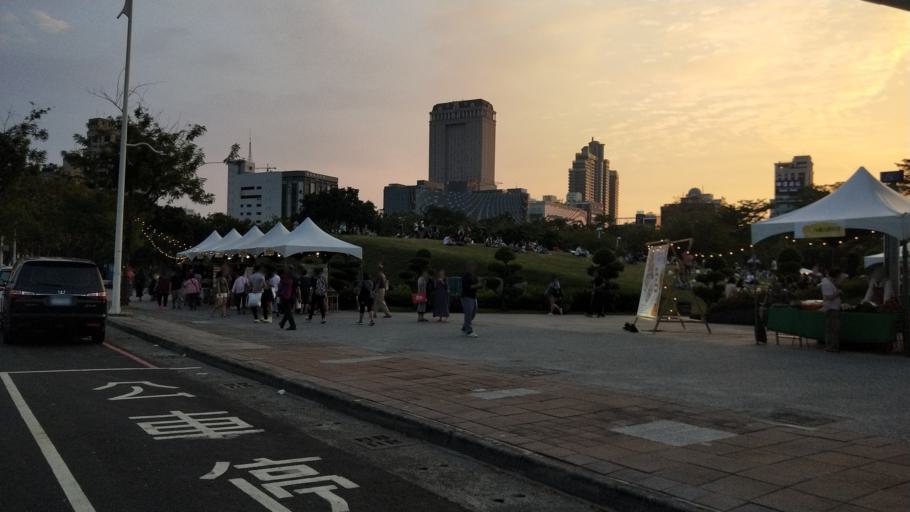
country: TW
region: Kaohsiung
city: Kaohsiung
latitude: 22.6247
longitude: 120.3011
